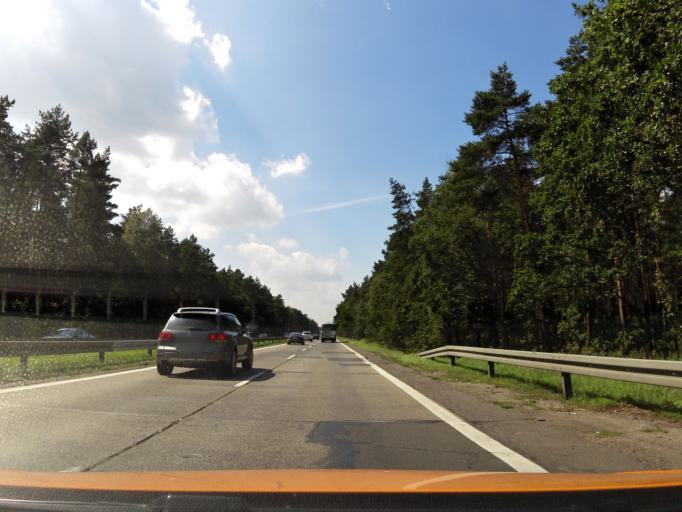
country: PL
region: West Pomeranian Voivodeship
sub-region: Powiat gryfinski
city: Stare Czarnowo
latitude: 53.4166
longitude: 14.7480
